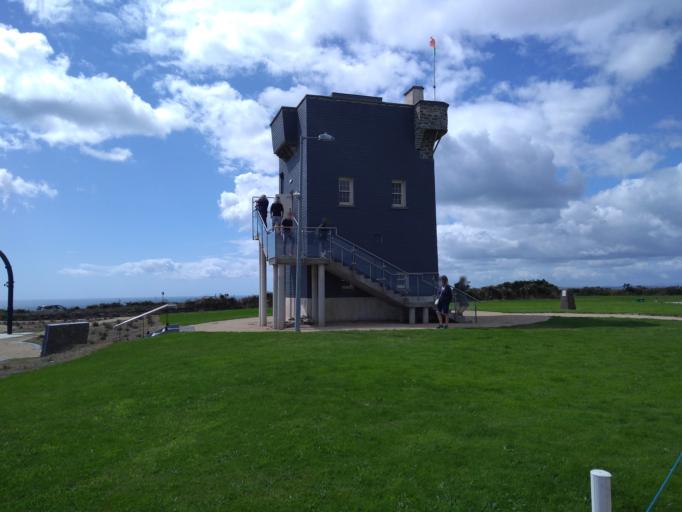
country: IE
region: Munster
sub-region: County Cork
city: Kinsale
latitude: 51.6202
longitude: -8.5424
